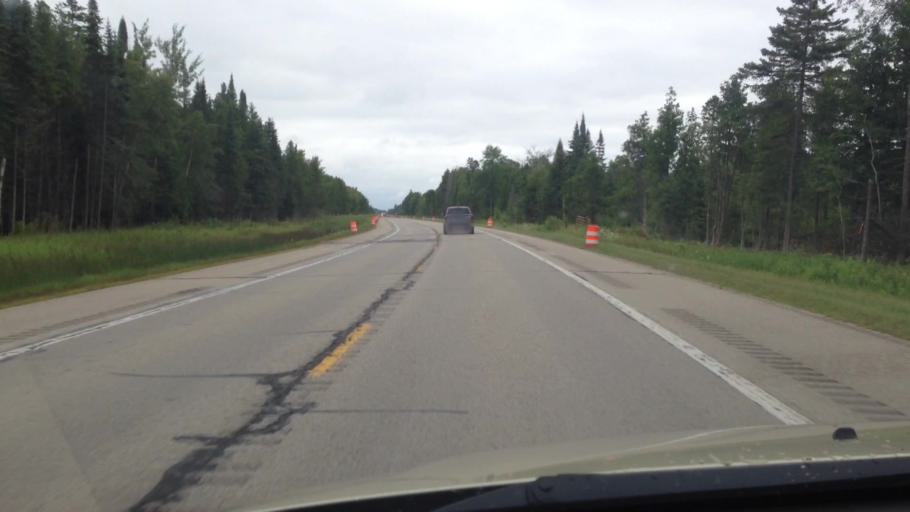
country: US
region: Michigan
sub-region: Delta County
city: Escanaba
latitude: 45.5994
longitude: -87.2261
